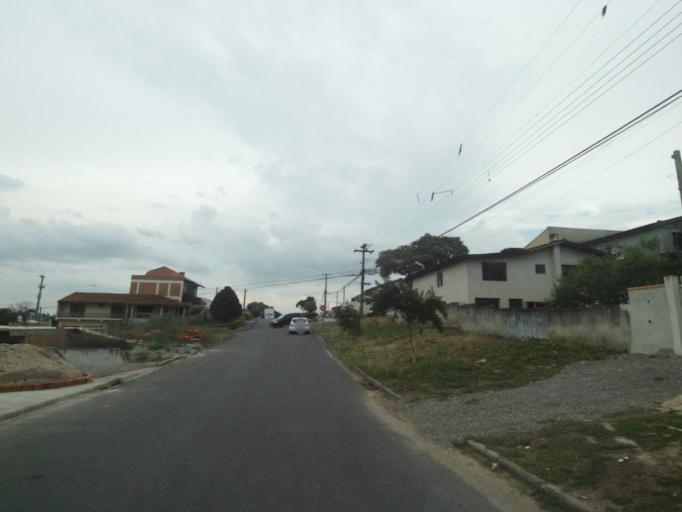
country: BR
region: Parana
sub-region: Pinhais
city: Pinhais
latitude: -25.3981
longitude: -49.2066
